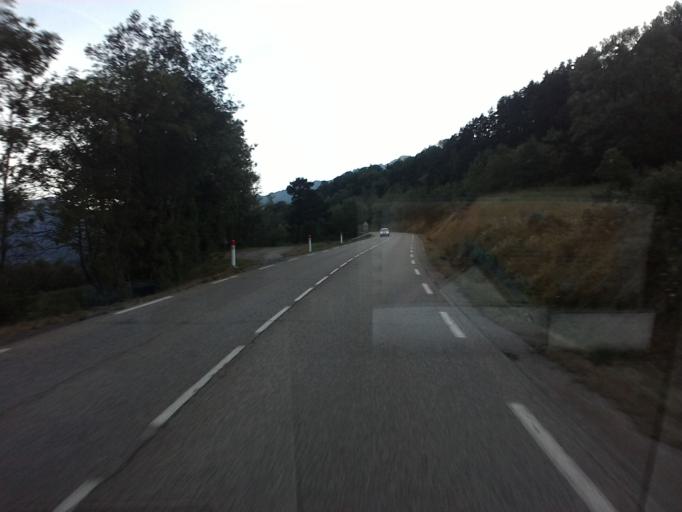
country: FR
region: Provence-Alpes-Cote d'Azur
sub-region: Departement des Hautes-Alpes
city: Saint-Bonnet-en-Champsaur
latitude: 44.7374
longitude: 6.0053
